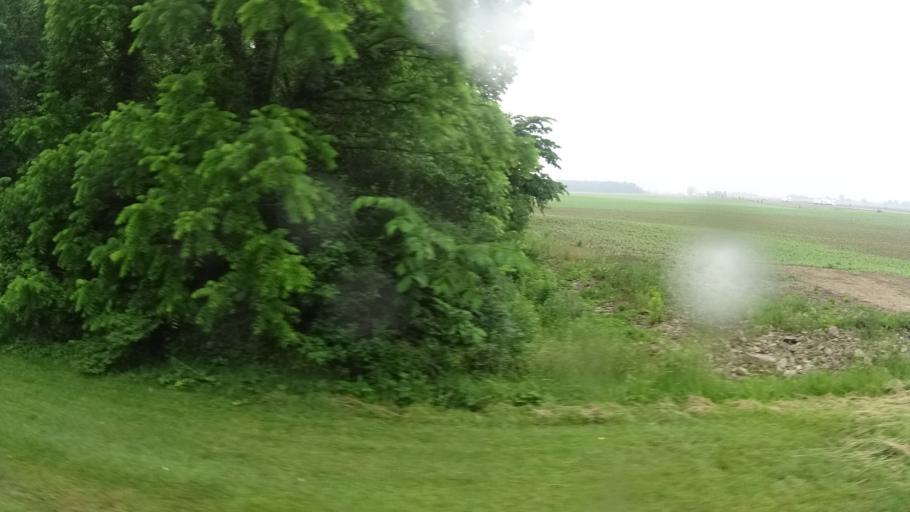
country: US
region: Ohio
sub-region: Huron County
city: Bellevue
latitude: 41.3486
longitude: -82.8440
